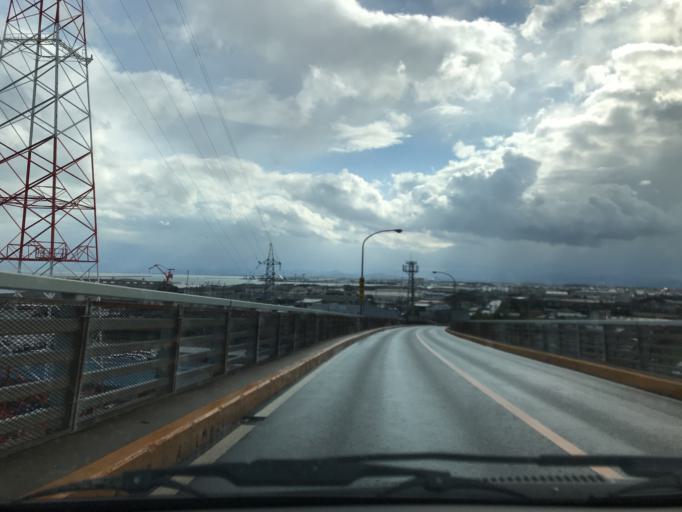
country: JP
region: Shimane
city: Sakaiminato
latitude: 35.5466
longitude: 133.2456
